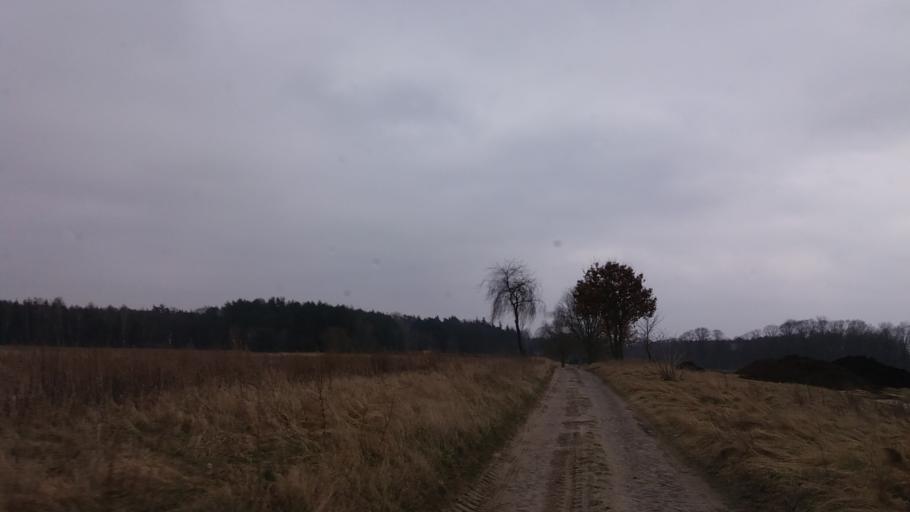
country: PL
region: West Pomeranian Voivodeship
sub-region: Powiat choszczenski
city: Recz
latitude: 53.1834
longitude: 15.5160
